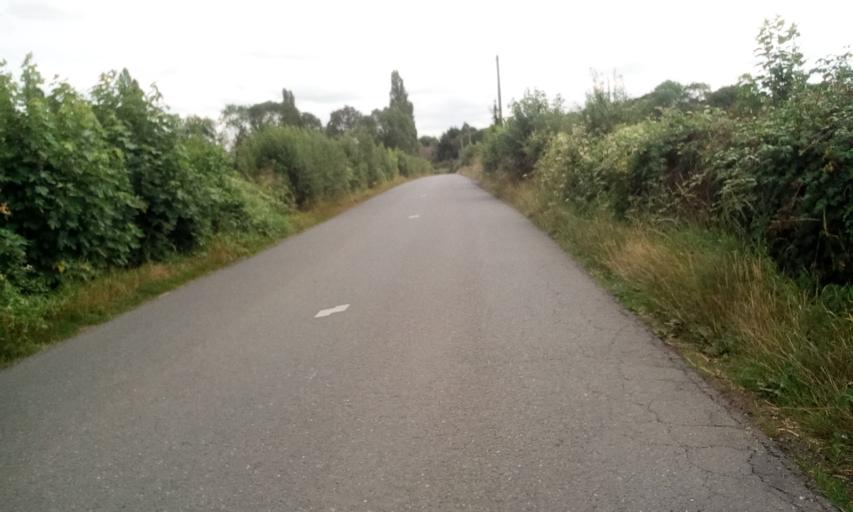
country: FR
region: Lower Normandy
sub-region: Departement du Calvados
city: Bavent
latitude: 49.2483
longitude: -0.1882
